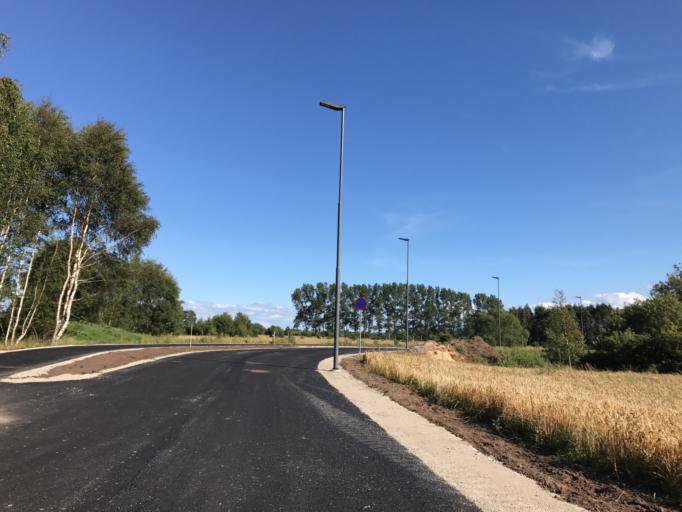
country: SE
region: Skane
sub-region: Bastads Kommun
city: Bastad
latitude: 56.4455
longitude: 12.9081
